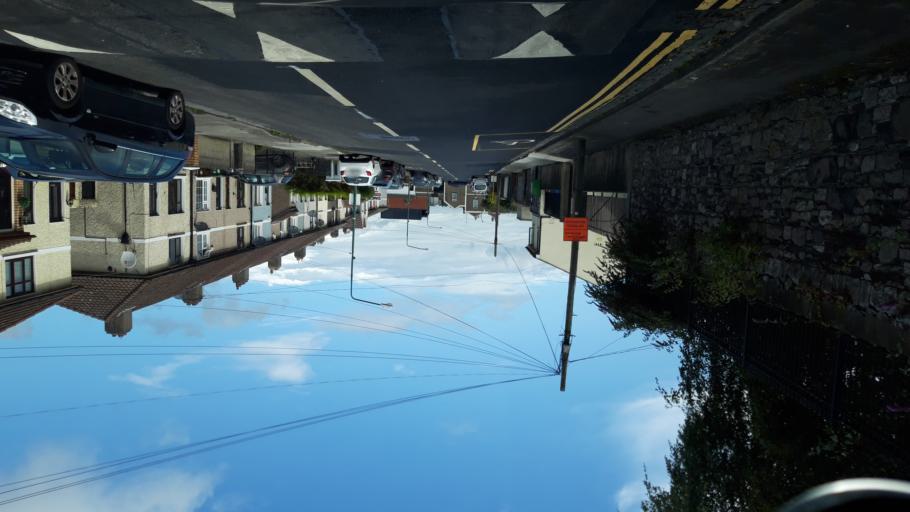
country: IE
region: Leinster
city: Ringsend
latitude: 53.3520
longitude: -6.2361
